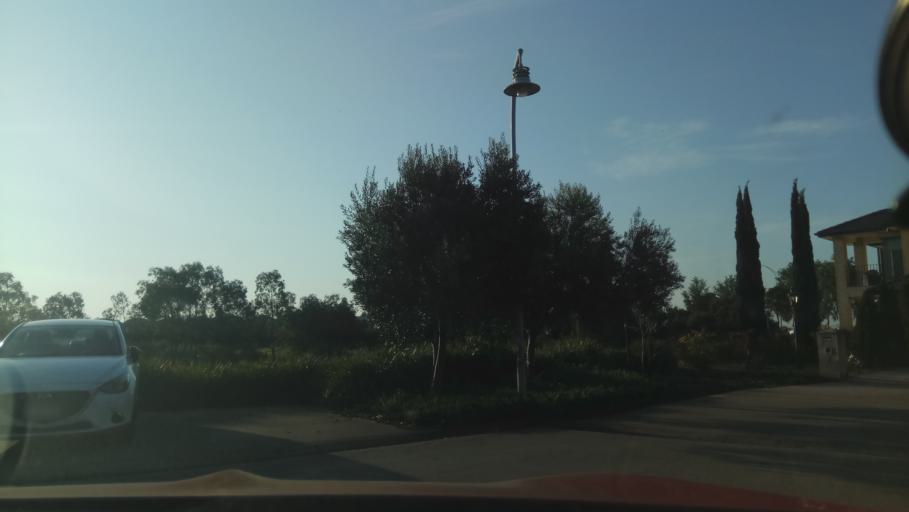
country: AU
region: Victoria
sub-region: Hobsons Bay
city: Altona Meadows
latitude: -37.8877
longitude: 144.7695
